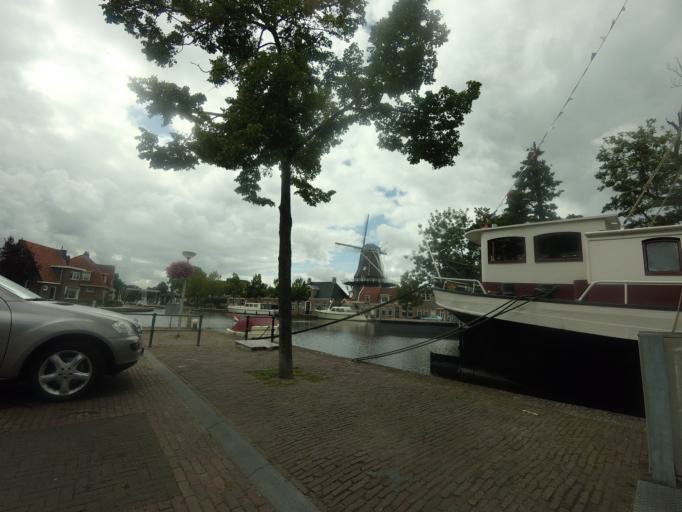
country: NL
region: Drenthe
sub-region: Gemeente Meppel
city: Meppel
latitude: 52.6955
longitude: 6.1877
